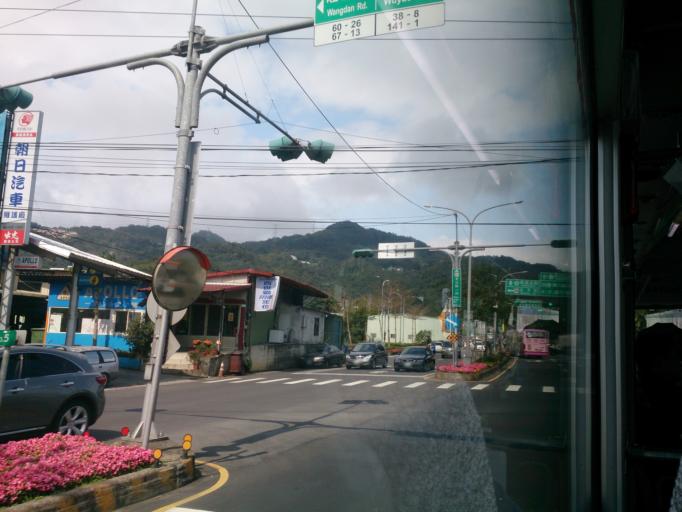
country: TW
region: Taipei
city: Taipei
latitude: 25.0052
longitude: 121.6307
